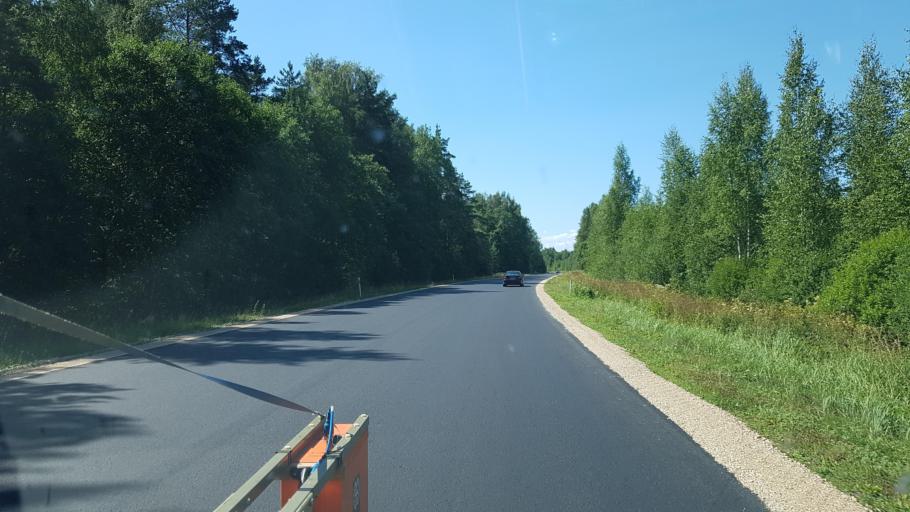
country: EE
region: Ida-Virumaa
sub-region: Kohtla-Nomme vald
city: Kohtla-Nomme
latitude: 59.0445
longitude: 27.2608
